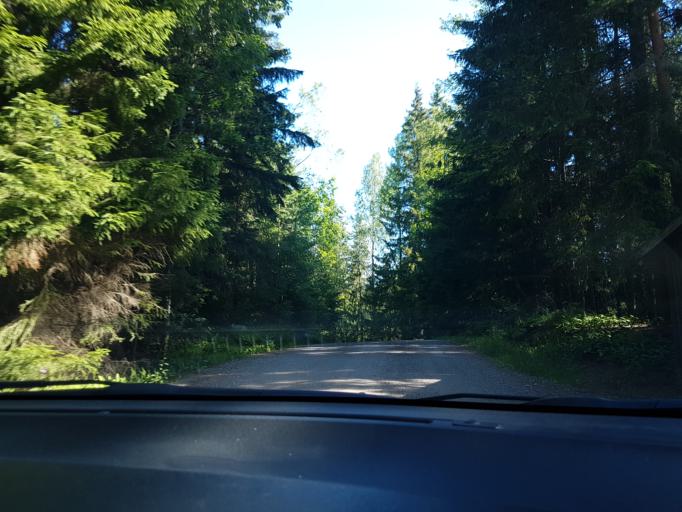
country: FI
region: Uusimaa
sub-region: Helsinki
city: Sibbo
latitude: 60.2899
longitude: 25.2406
